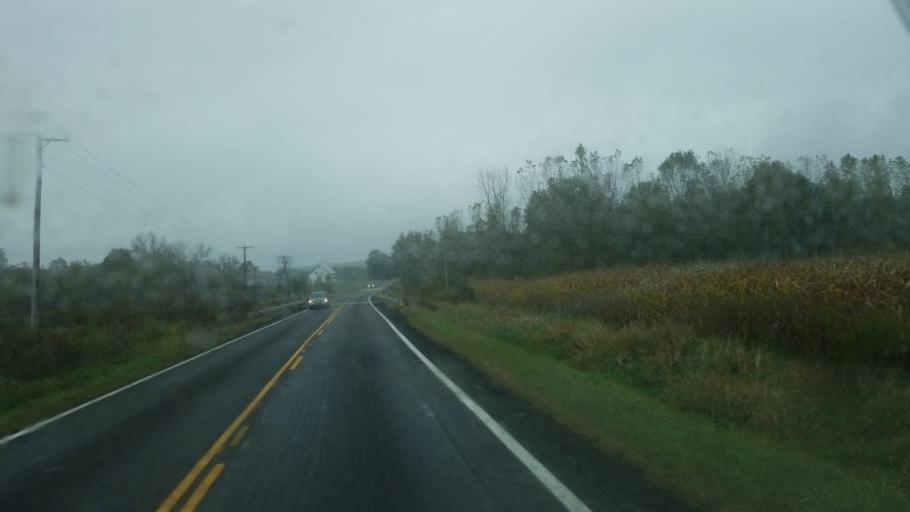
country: US
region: Ohio
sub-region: Richland County
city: Lexington
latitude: 40.6159
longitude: -82.5899
